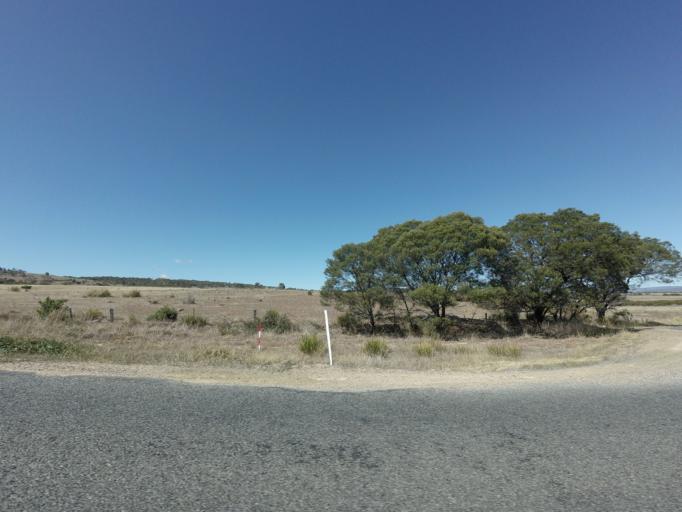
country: AU
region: Tasmania
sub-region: Break O'Day
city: St Helens
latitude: -41.9978
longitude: 148.0908
